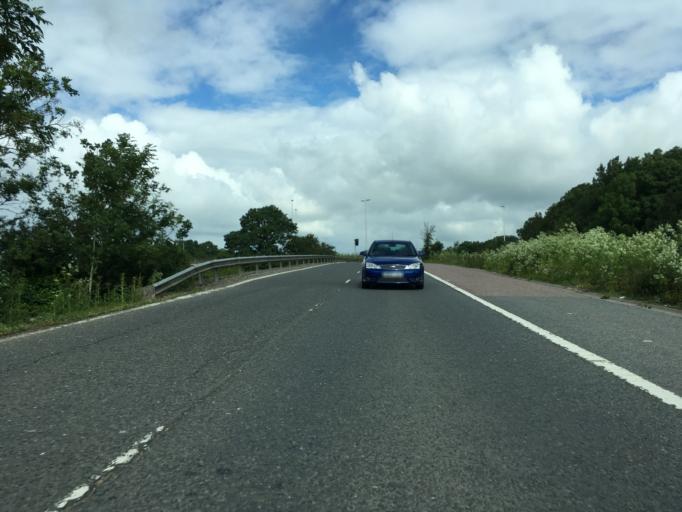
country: GB
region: England
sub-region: Wiltshire
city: Lydiard Tregoze
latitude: 51.5449
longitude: -1.8511
